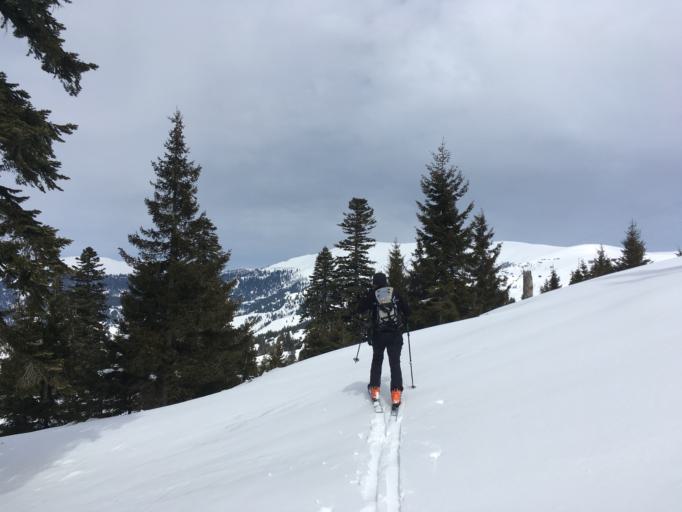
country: GE
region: Ajaria
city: Dioknisi
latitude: 41.6216
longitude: 42.4943
